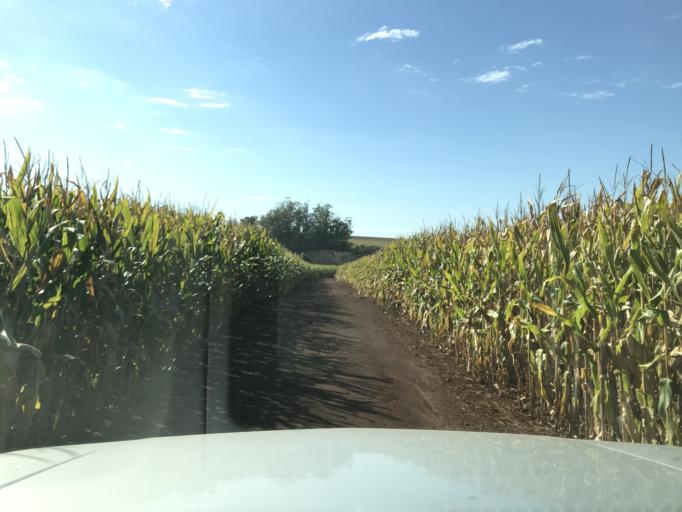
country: BR
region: Parana
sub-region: Palotina
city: Palotina
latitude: -24.2639
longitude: -53.8071
